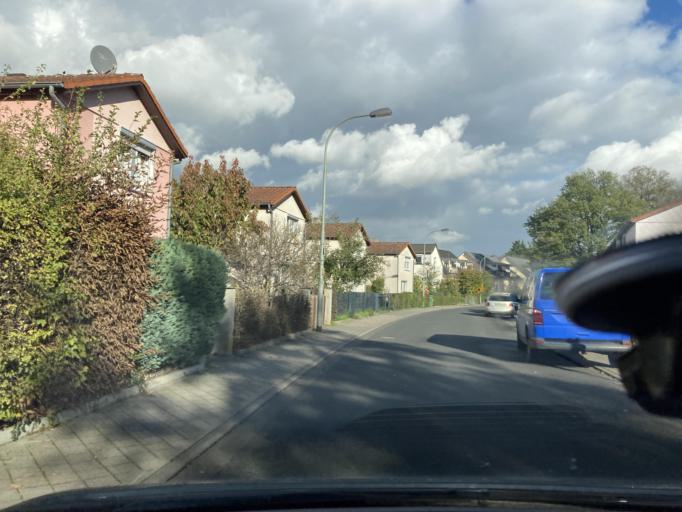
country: DE
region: Hesse
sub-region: Regierungsbezirk Darmstadt
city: Frankfurt am Main
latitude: 50.1675
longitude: 8.6723
